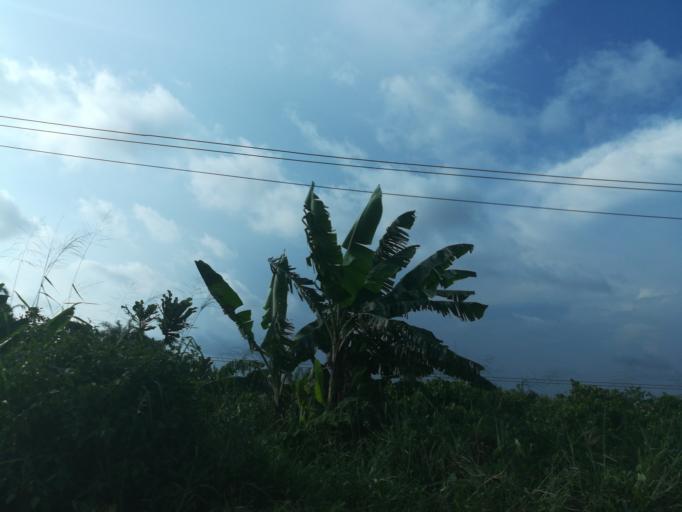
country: NG
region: Ogun
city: Ado Odo
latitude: 6.4931
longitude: 3.0806
